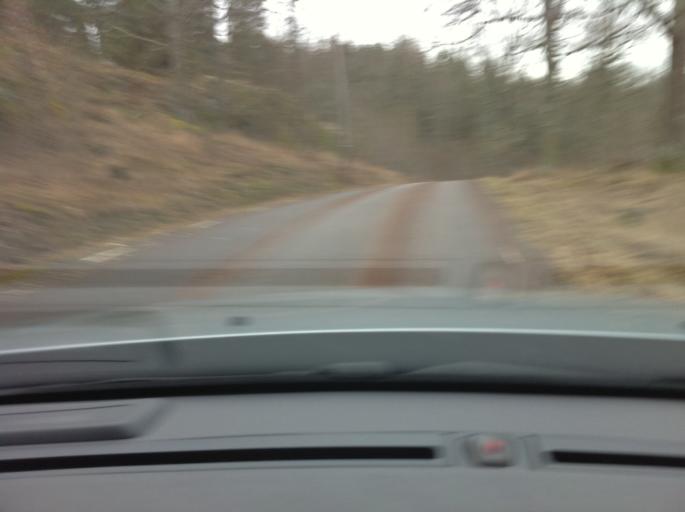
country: SE
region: Kalmar
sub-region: Vasterviks Kommun
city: Forserum
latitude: 57.9300
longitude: 16.5218
